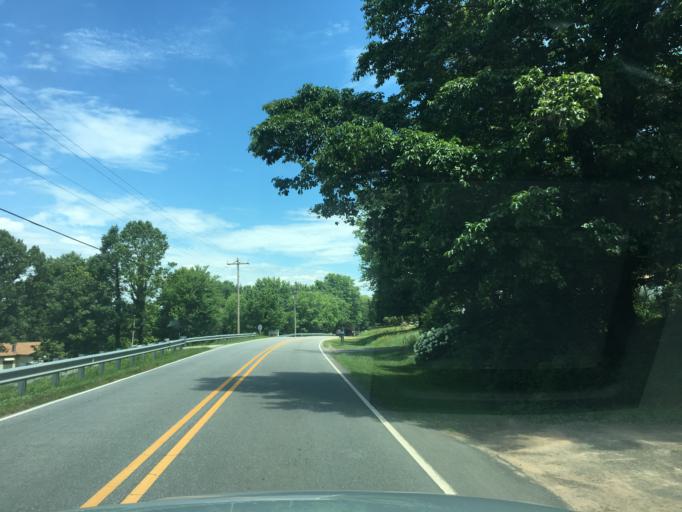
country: US
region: North Carolina
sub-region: Burke County
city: Glen Alpine
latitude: 35.6610
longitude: -81.7818
